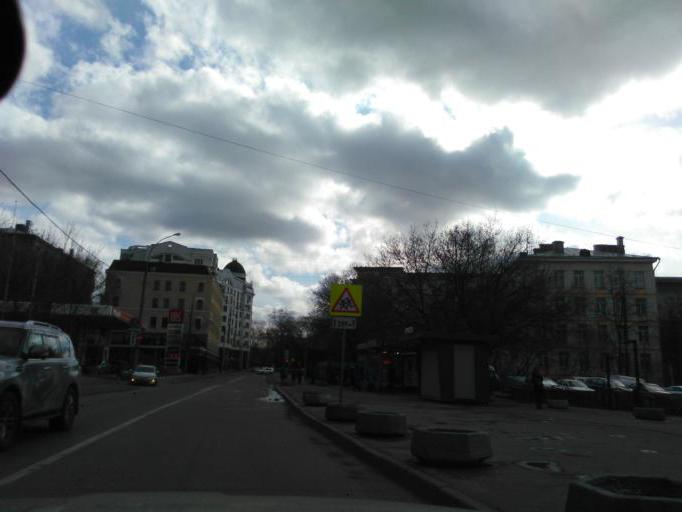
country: RU
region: Moskovskaya
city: Dorogomilovo
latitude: 55.7571
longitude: 37.5665
